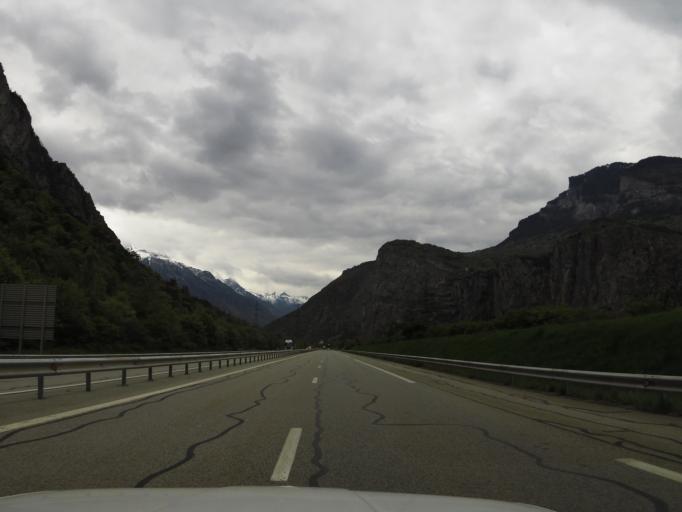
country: FR
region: Rhone-Alpes
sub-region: Departement de la Savoie
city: Saint-Jean-de-Maurienne
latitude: 45.3049
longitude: 6.3460
